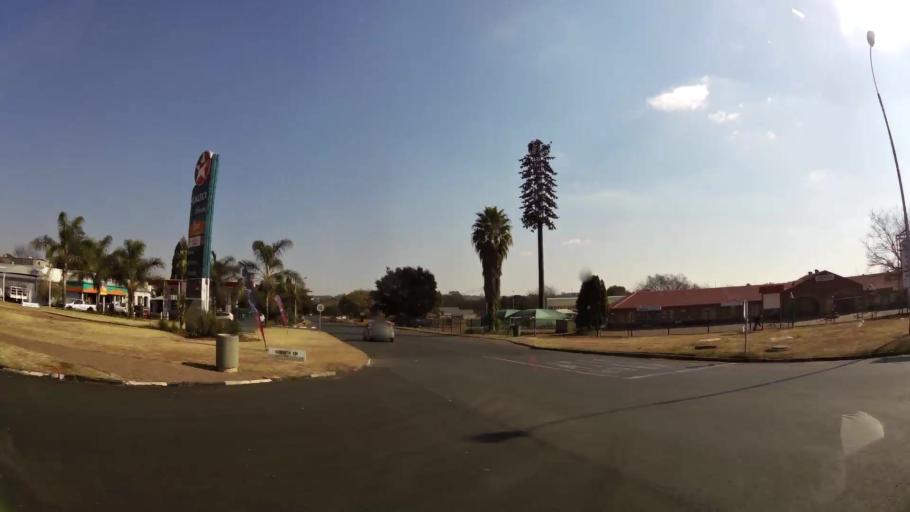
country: ZA
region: Gauteng
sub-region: West Rand District Municipality
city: Randfontein
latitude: -26.1601
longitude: 27.6934
